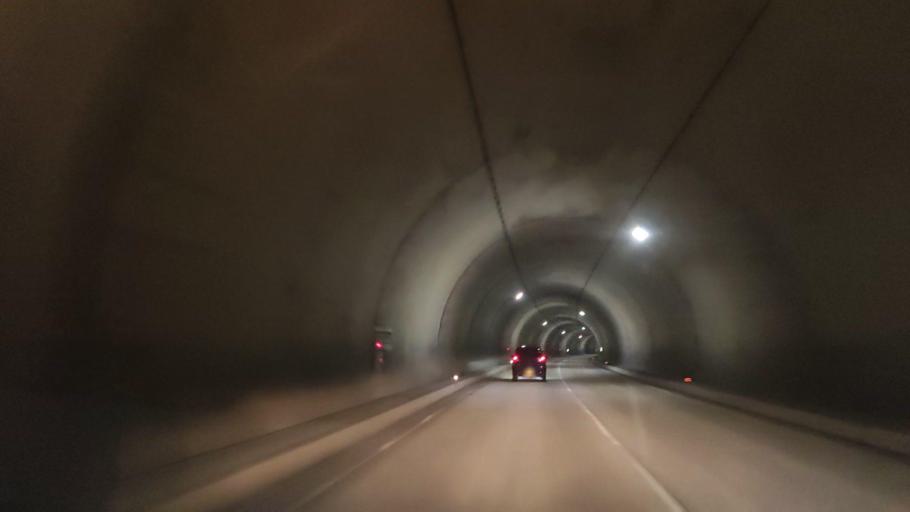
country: JP
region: Tottori
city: Kurayoshi
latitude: 35.4125
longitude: 133.8525
